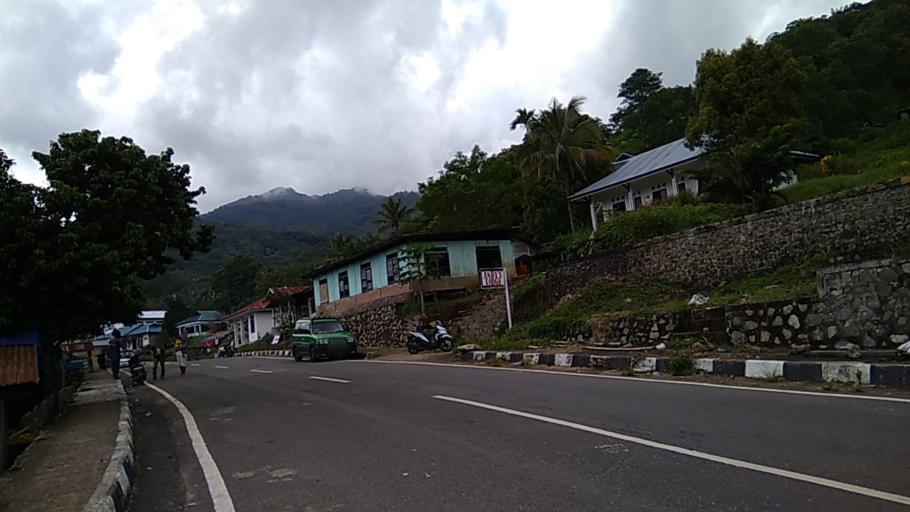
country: ID
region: East Nusa Tenggara
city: Koanara
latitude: -8.7497
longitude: 121.8493
